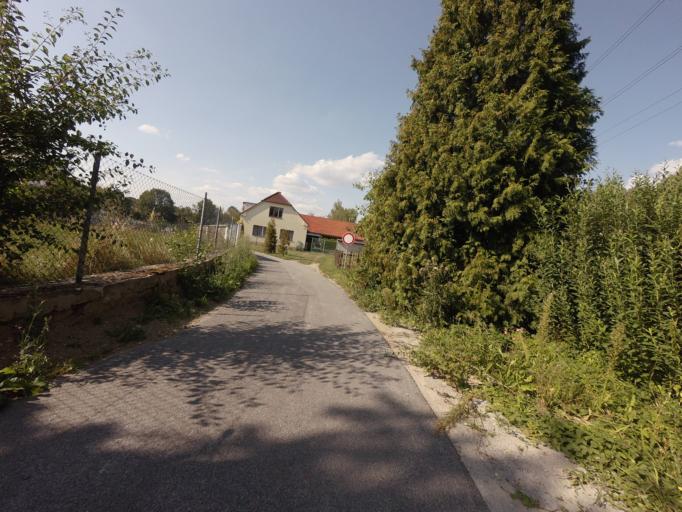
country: CZ
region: Jihocesky
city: Tyn nad Vltavou
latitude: 49.1937
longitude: 14.4455
